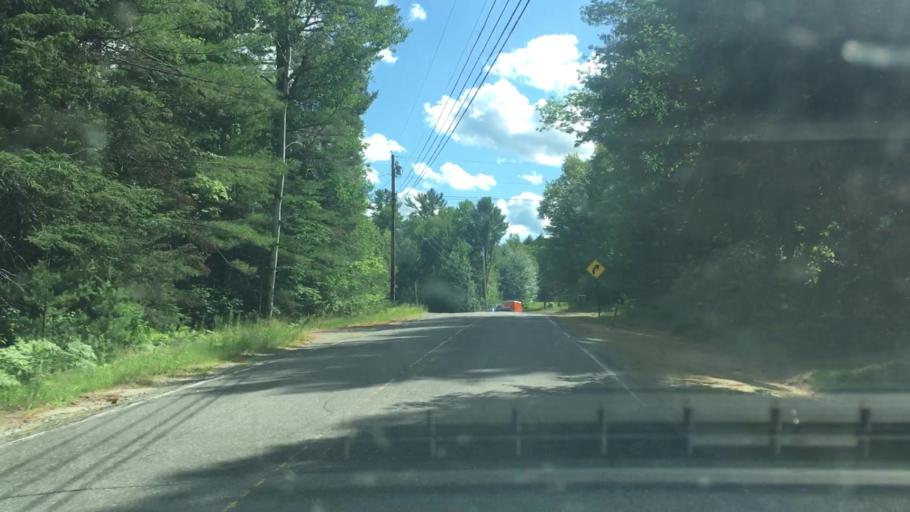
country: US
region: Maine
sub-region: Franklin County
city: Farmington
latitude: 44.7106
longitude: -70.0862
